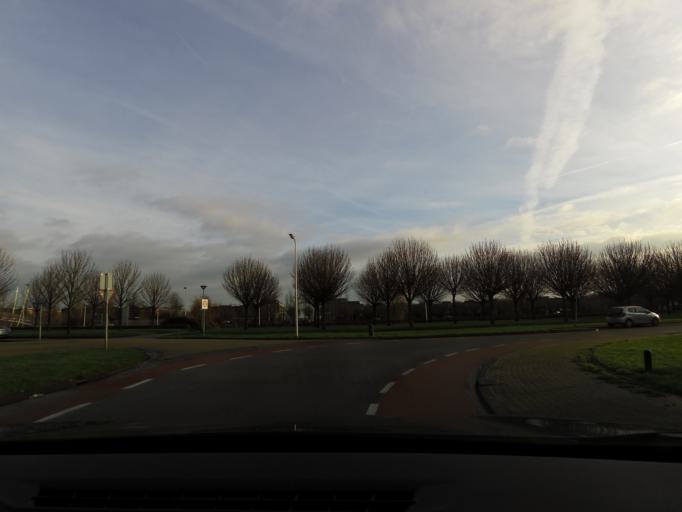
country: NL
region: South Holland
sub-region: Gemeente Hellevoetsluis
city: Nieuwenhoorn
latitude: 51.8451
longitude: 4.1611
